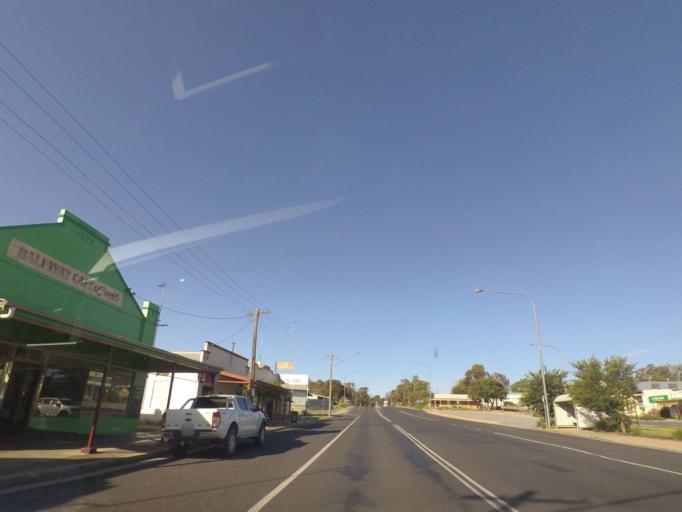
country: AU
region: New South Wales
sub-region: Wagga Wagga
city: Forest Hill
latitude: -35.2767
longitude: 147.7373
